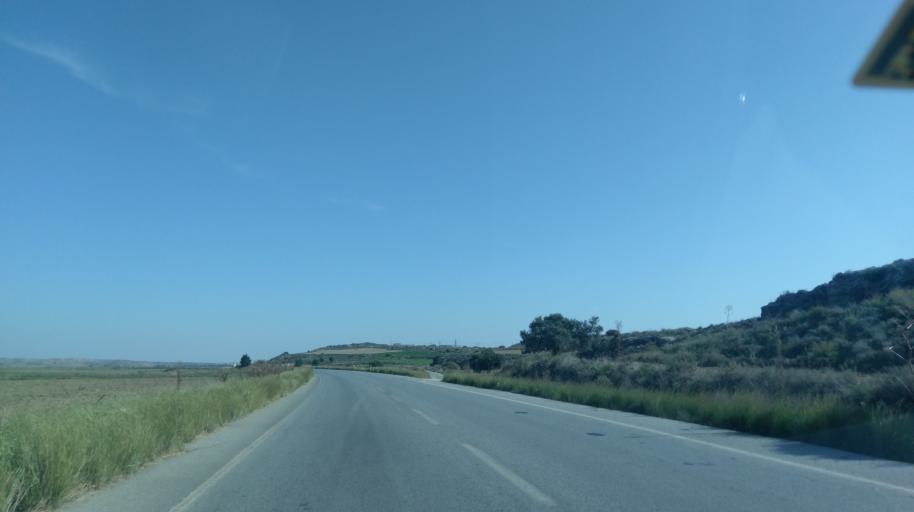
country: CY
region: Ammochostos
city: Lefkonoiko
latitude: 35.2684
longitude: 33.8089
